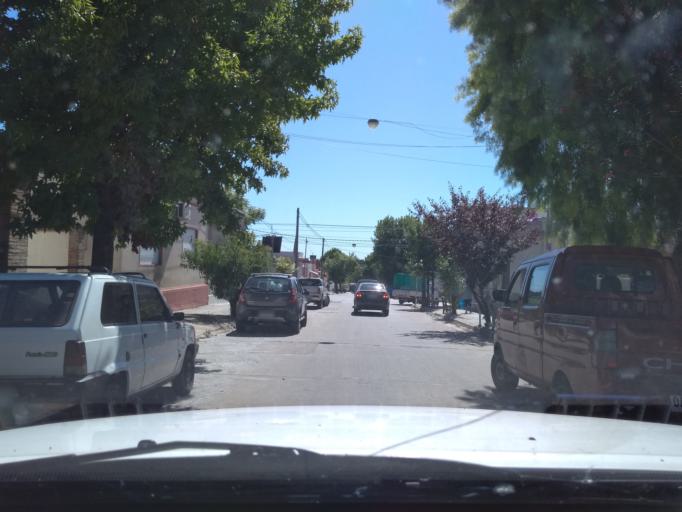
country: UY
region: Florida
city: Florida
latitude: -34.0929
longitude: -56.2152
